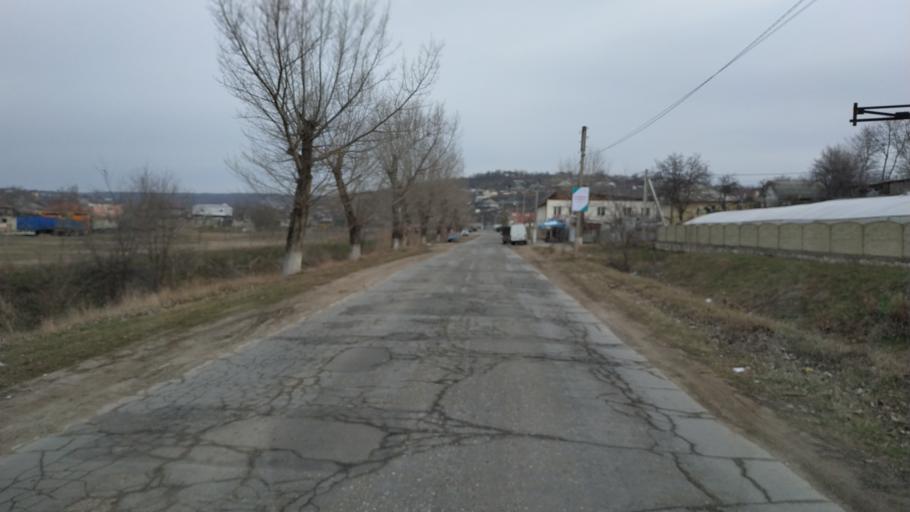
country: MD
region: Chisinau
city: Vatra
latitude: 47.0857
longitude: 28.7706
